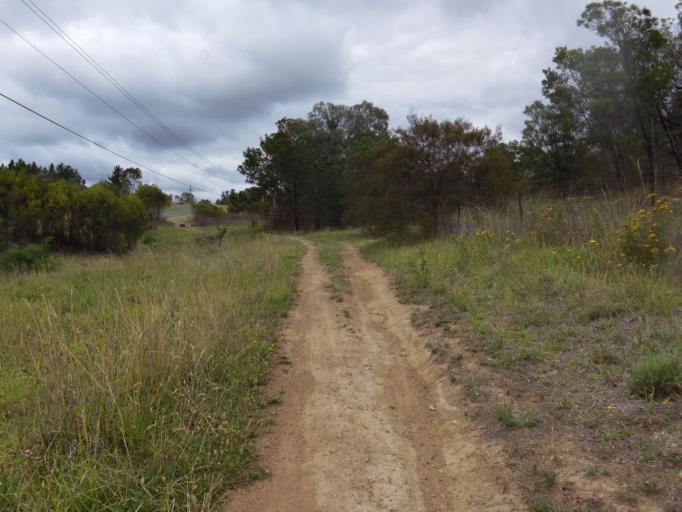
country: AU
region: Australian Capital Territory
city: Macquarie
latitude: -35.3287
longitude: 149.0260
